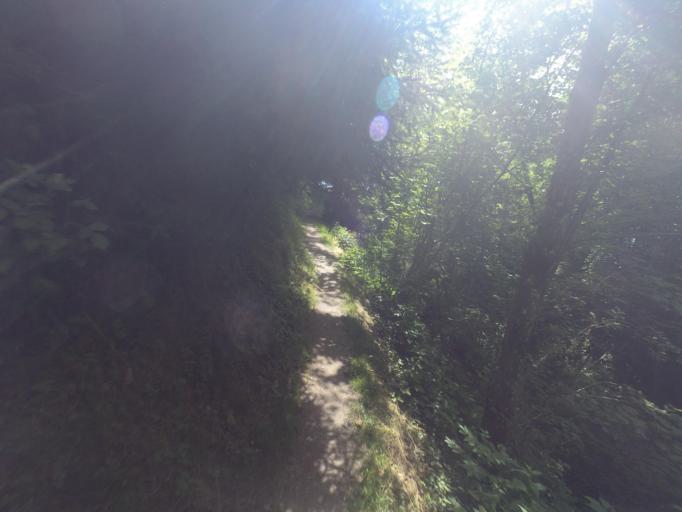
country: AT
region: Salzburg
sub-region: Politischer Bezirk Sankt Johann im Pongau
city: Sankt Veit im Pongau
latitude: 47.3297
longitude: 13.1402
